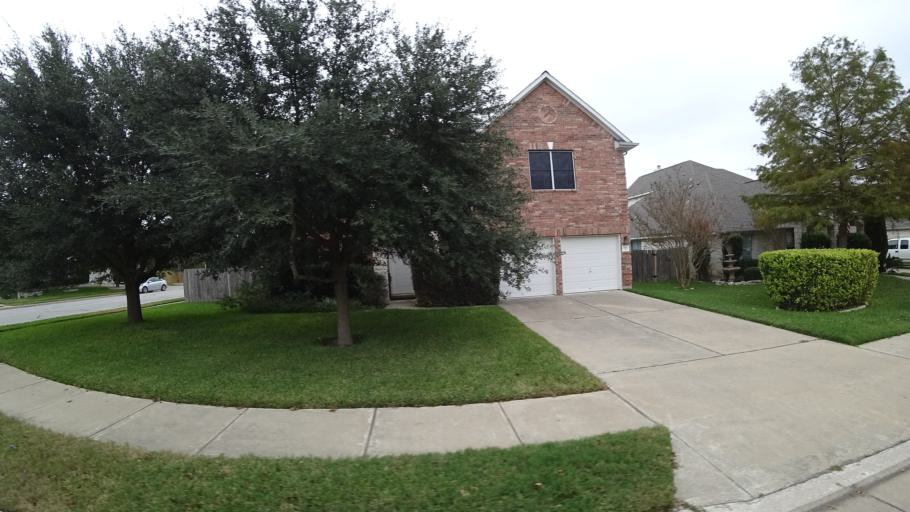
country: US
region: Texas
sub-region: Travis County
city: Pflugerville
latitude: 30.4291
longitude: -97.6161
